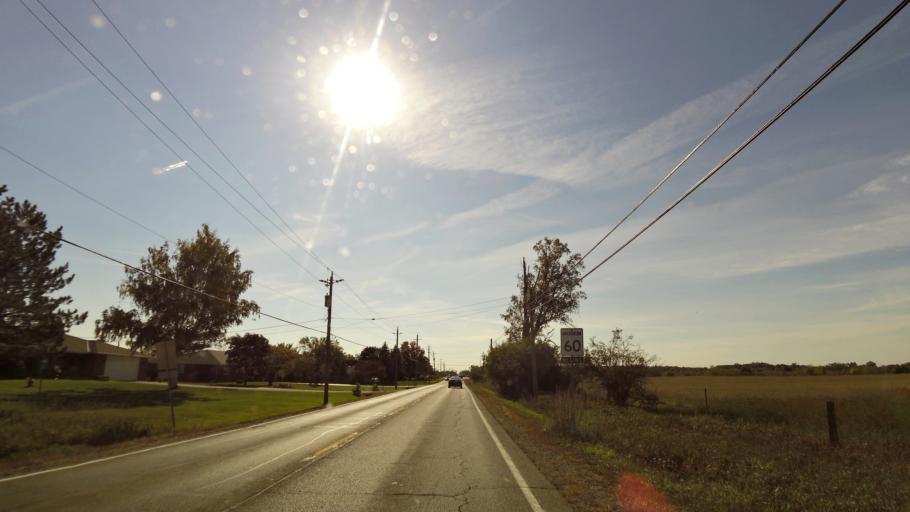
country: CA
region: Ontario
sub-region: Halton
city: Milton
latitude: 43.5387
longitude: -79.7777
